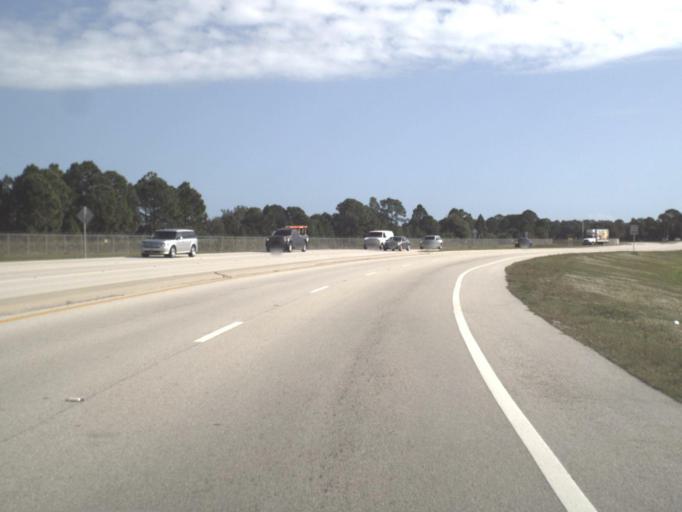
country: US
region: Florida
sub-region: Brevard County
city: June Park
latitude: 28.0996
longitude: -80.6711
